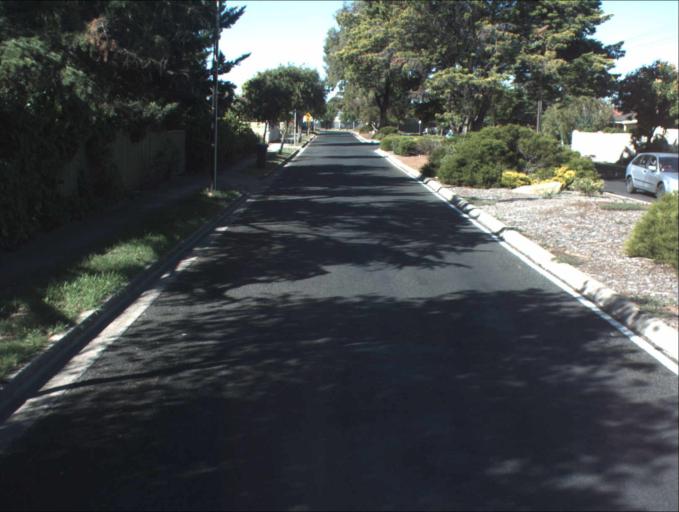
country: AU
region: South Australia
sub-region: Port Adelaide Enfield
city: Klemzig
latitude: -34.8770
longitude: 138.6146
